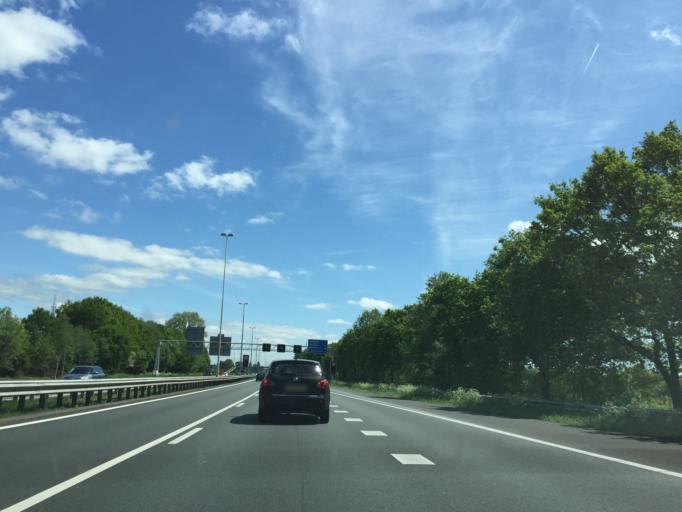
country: NL
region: Utrecht
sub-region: Gemeente Leusden
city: Leusden
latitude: 52.1675
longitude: 5.4481
